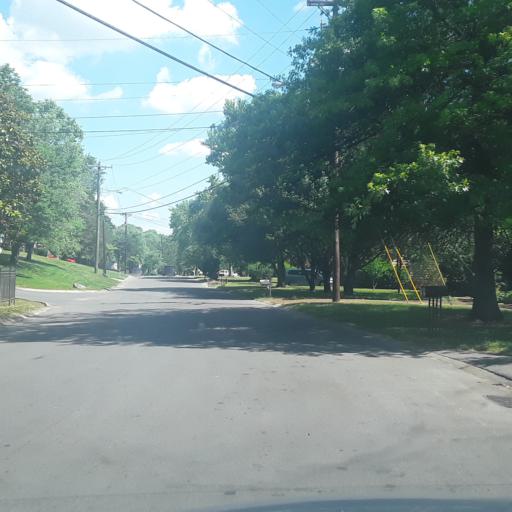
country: US
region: Tennessee
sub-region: Williamson County
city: Brentwood Estates
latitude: 36.0379
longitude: -86.7027
